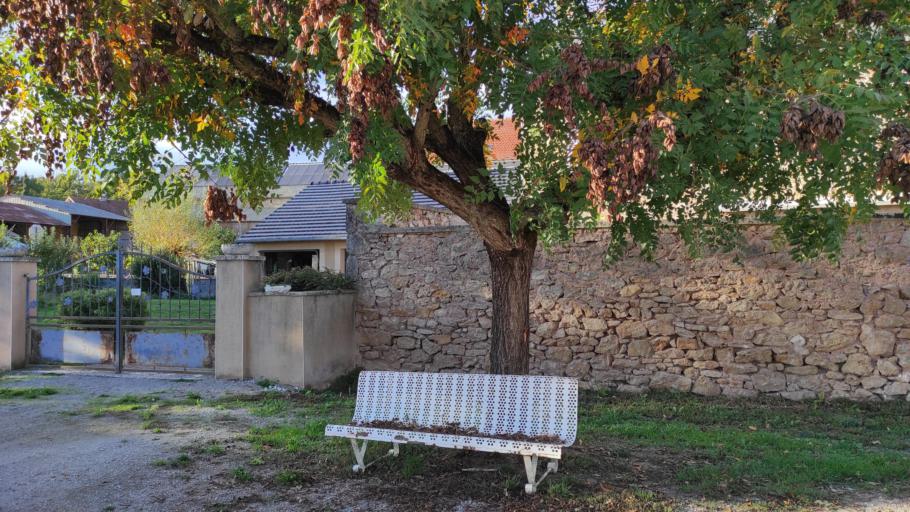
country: FR
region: Midi-Pyrenees
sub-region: Departement de l'Aveyron
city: Montbazens
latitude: 44.4226
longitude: 2.2190
